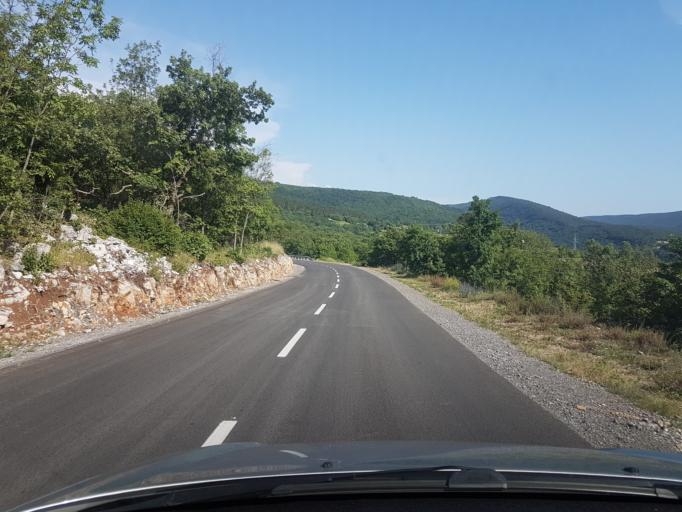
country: SI
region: Sezana
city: Sezana
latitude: 45.7629
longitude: 13.9354
